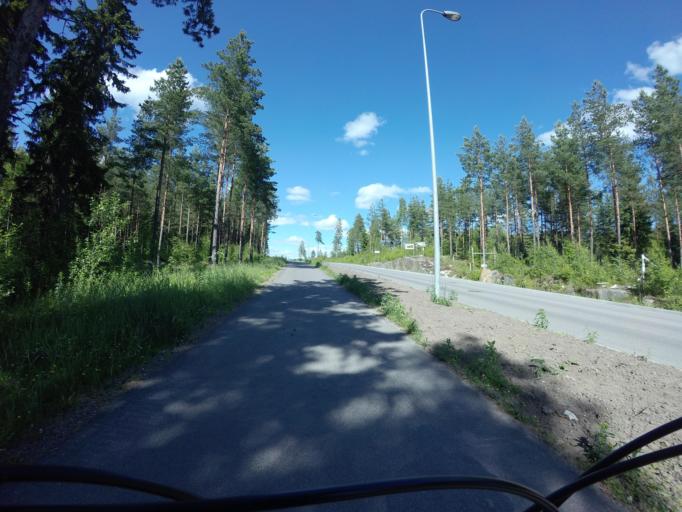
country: FI
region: Varsinais-Suomi
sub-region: Turku
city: Vahto
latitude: 60.5396
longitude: 22.3163
